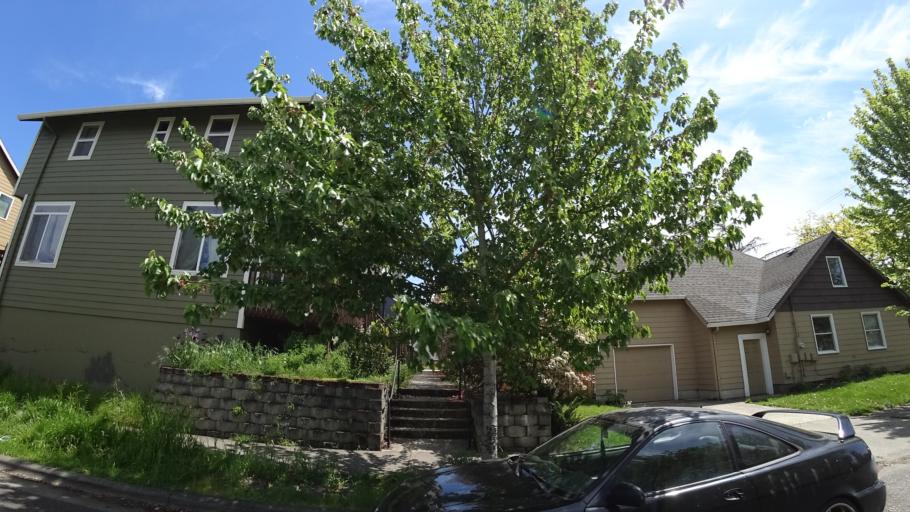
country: US
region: Oregon
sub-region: Washington County
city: Aloha
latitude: 45.4913
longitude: -122.8566
